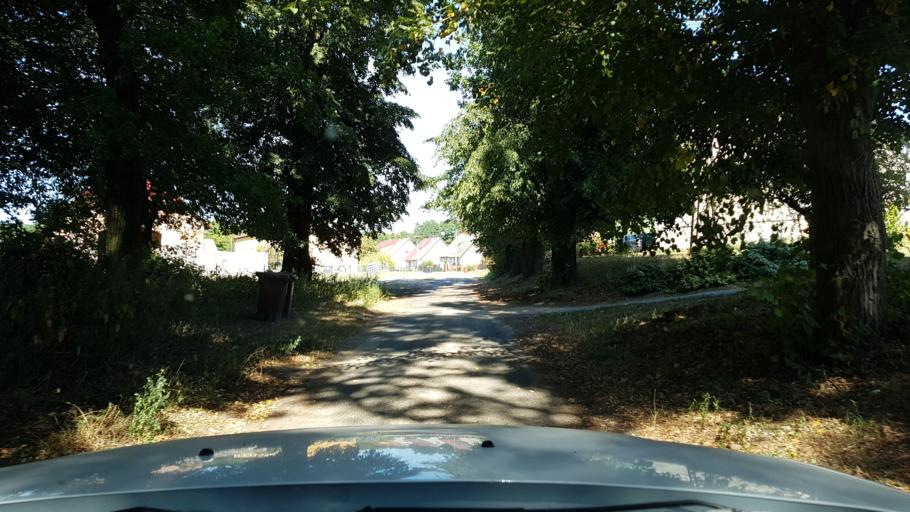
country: PL
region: West Pomeranian Voivodeship
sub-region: Powiat gryfinski
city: Cedynia
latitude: 52.8655
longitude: 14.2297
